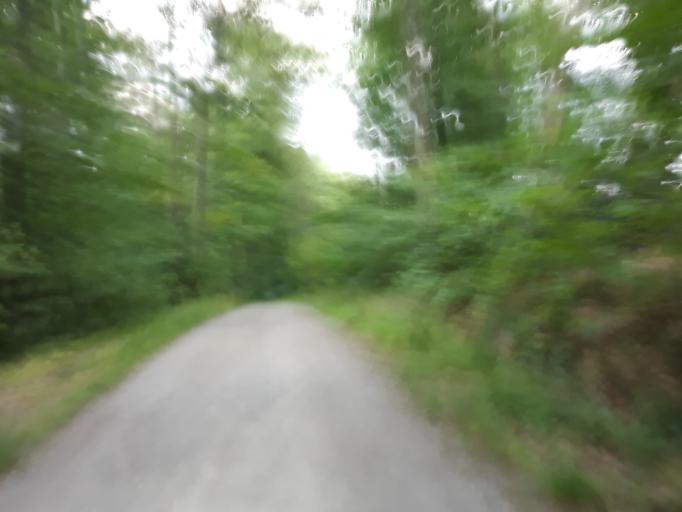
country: DE
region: Baden-Wuerttemberg
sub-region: Regierungsbezirk Stuttgart
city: Schonaich
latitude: 48.6701
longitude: 9.0565
